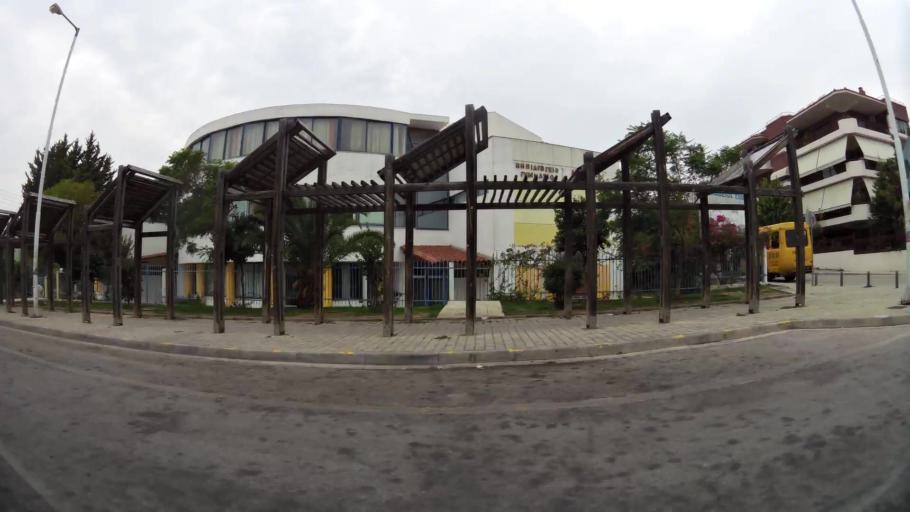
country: GR
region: Attica
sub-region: Nomarchia Athinas
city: Alimos
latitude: 37.9184
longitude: 23.7233
